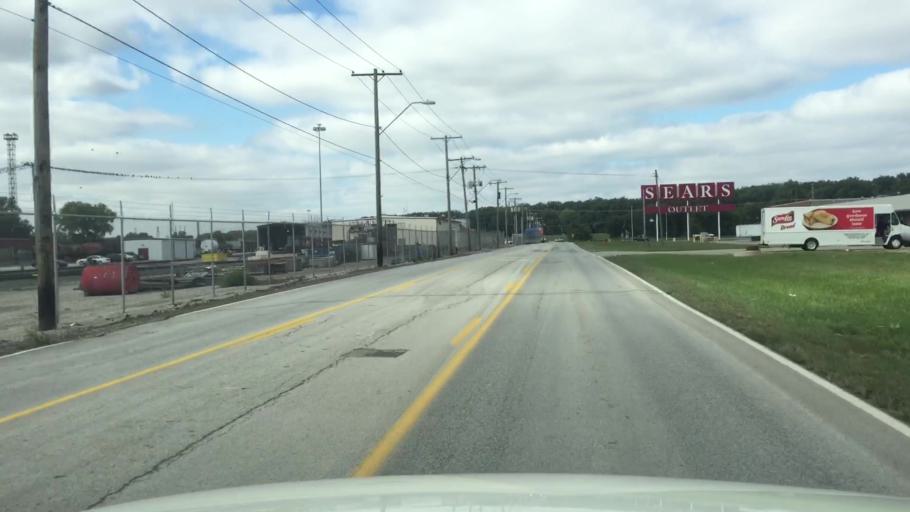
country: US
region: Missouri
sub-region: Clay County
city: North Kansas City
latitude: 39.1312
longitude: -94.5353
